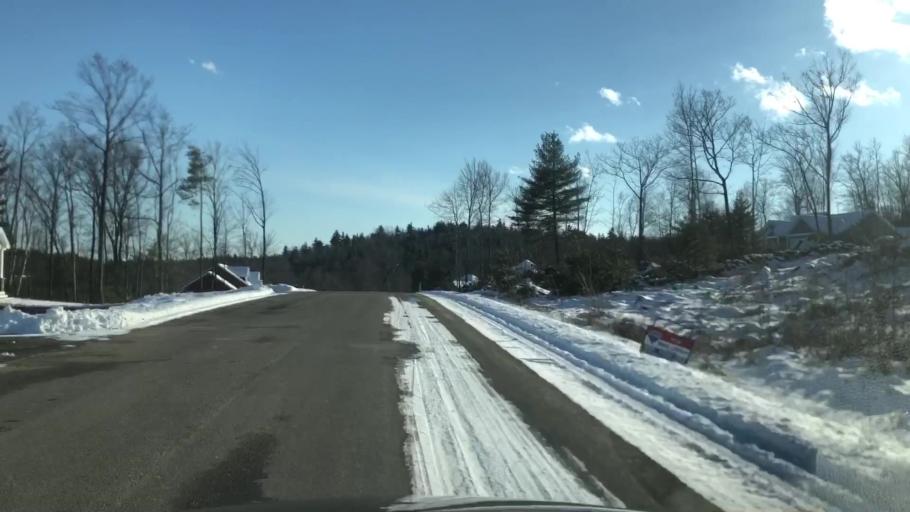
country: US
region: New Hampshire
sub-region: Hillsborough County
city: Wilton
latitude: 42.8045
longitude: -71.7104
